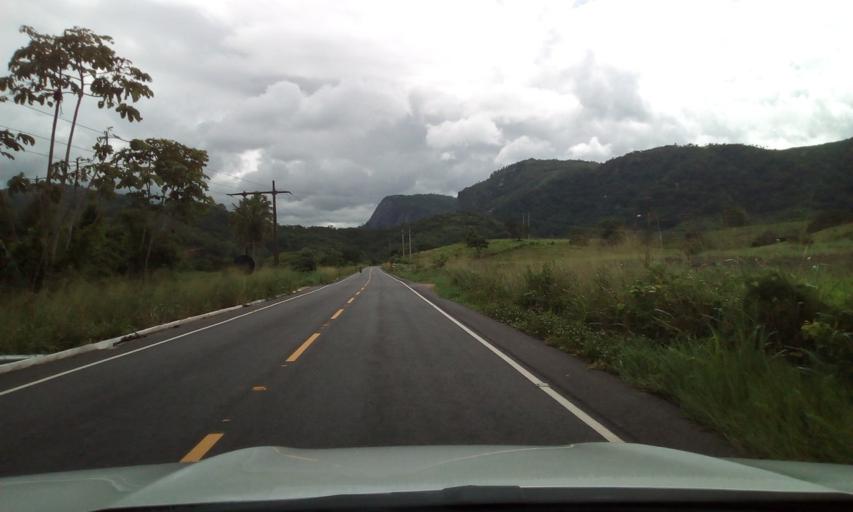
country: BR
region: Paraiba
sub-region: Alagoinha
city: Alagoinha
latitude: -6.8900
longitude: -35.5618
